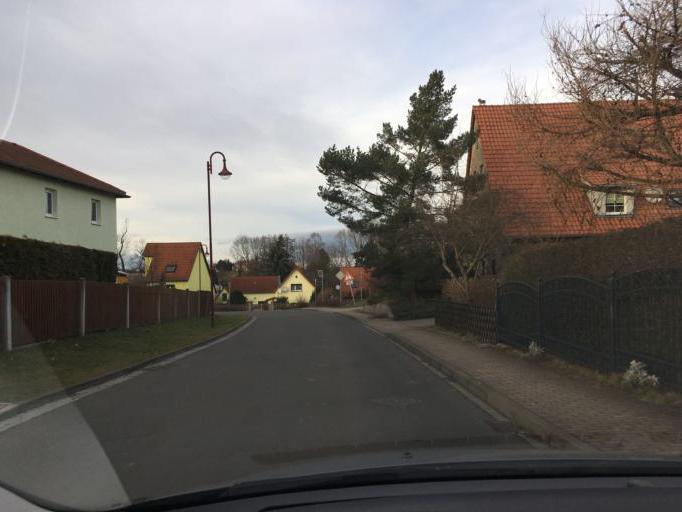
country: DE
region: Saxony
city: Grossposna
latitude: 51.2411
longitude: 12.4836
